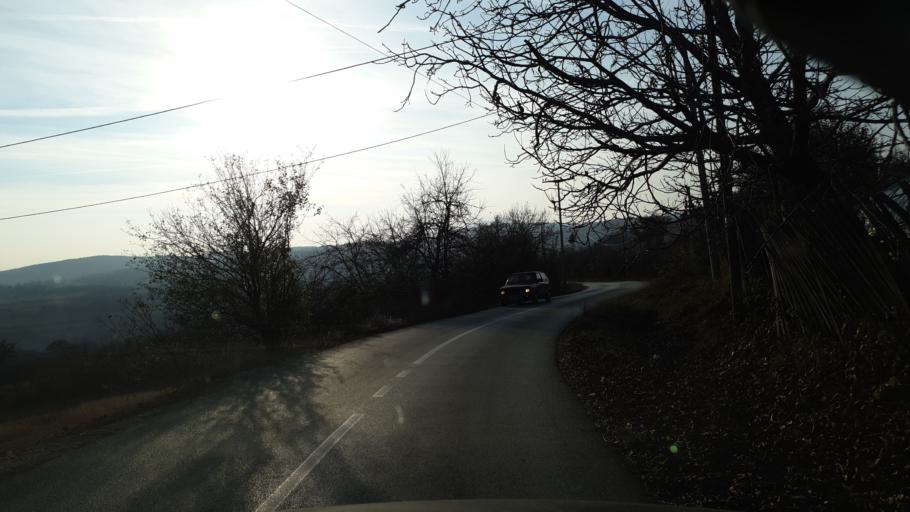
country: RS
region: Central Serbia
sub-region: Borski Okrug
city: Bor
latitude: 44.0489
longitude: 22.0893
